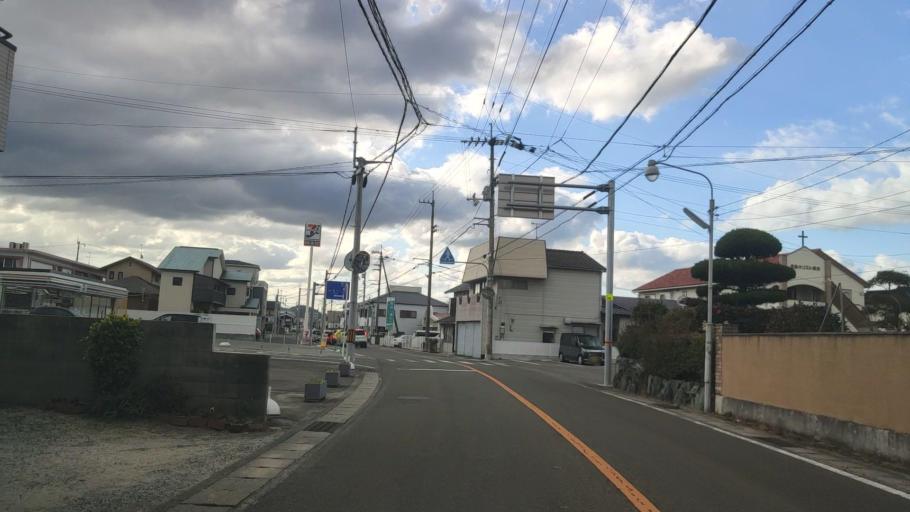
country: JP
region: Ehime
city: Hojo
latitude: 33.9731
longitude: 132.7732
